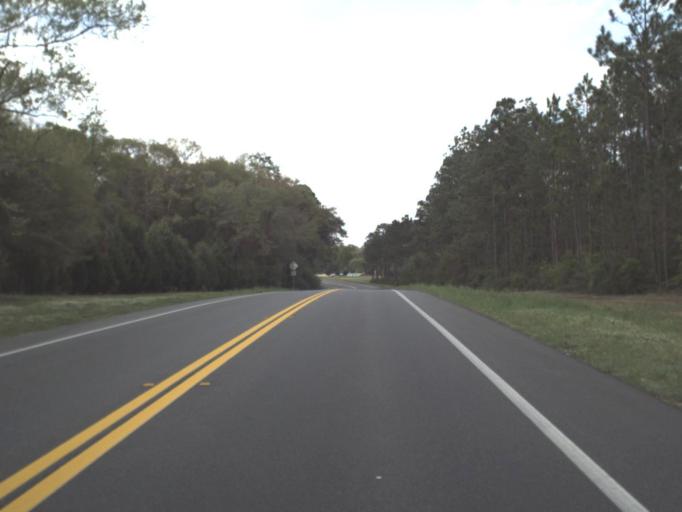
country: US
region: Florida
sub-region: Okaloosa County
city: Crestview
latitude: 30.8794
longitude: -86.5107
